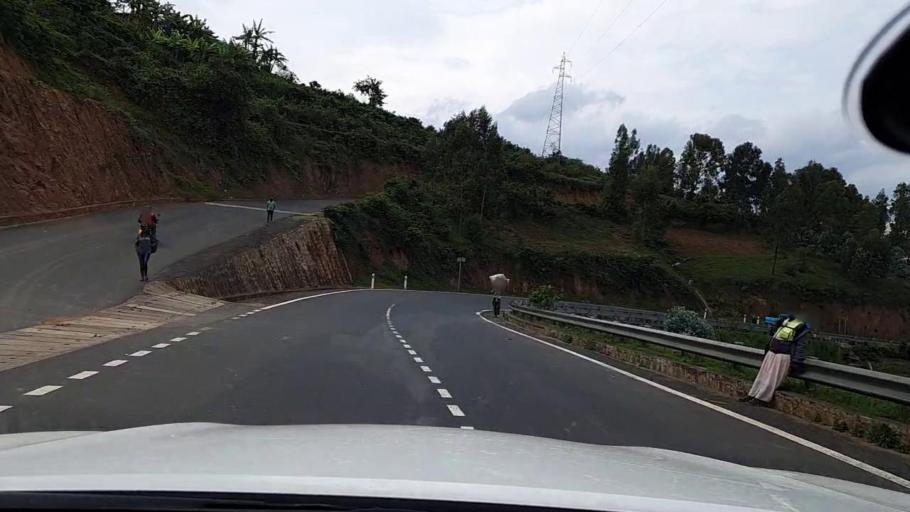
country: RW
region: Western Province
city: Kibuye
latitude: -2.1760
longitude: 29.2900
